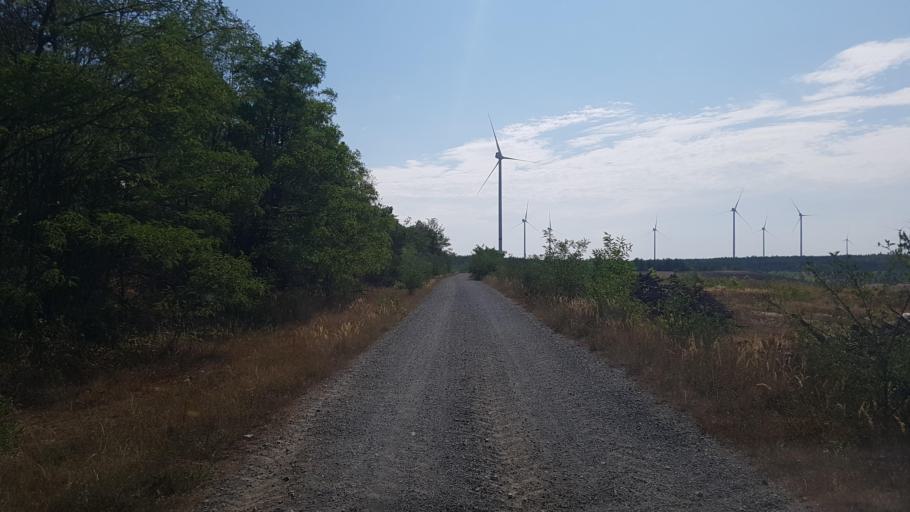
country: DE
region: Brandenburg
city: Schipkau
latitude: 51.5443
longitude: 13.8564
